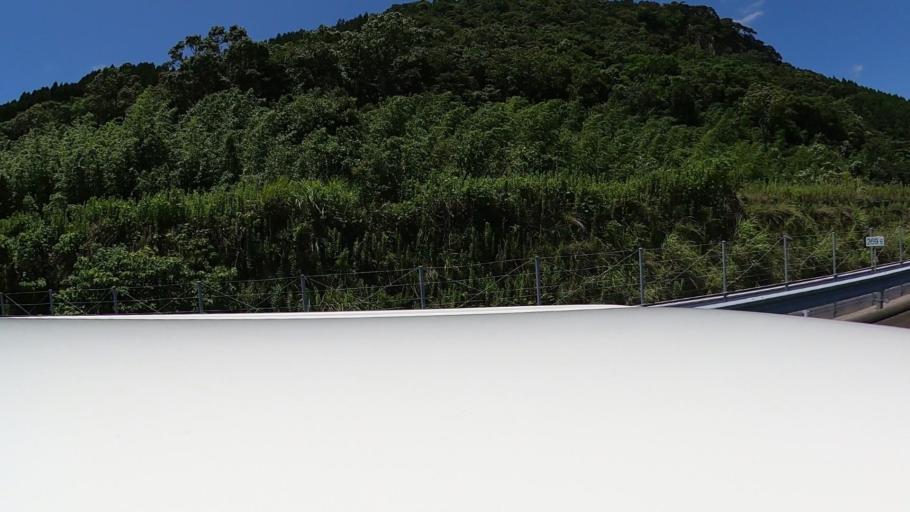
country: JP
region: Miyazaki
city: Nobeoka
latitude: 32.3897
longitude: 131.6221
